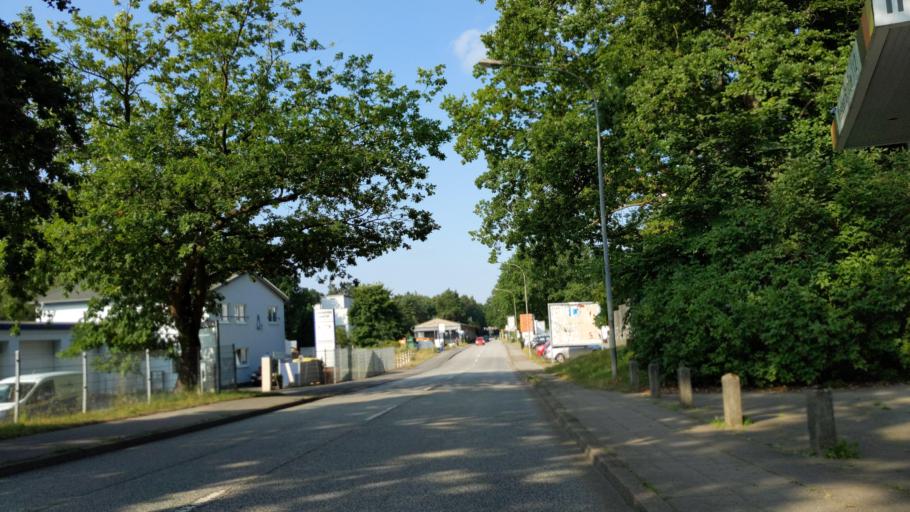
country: DE
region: Mecklenburg-Vorpommern
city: Selmsdorf
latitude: 53.8802
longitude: 10.7778
